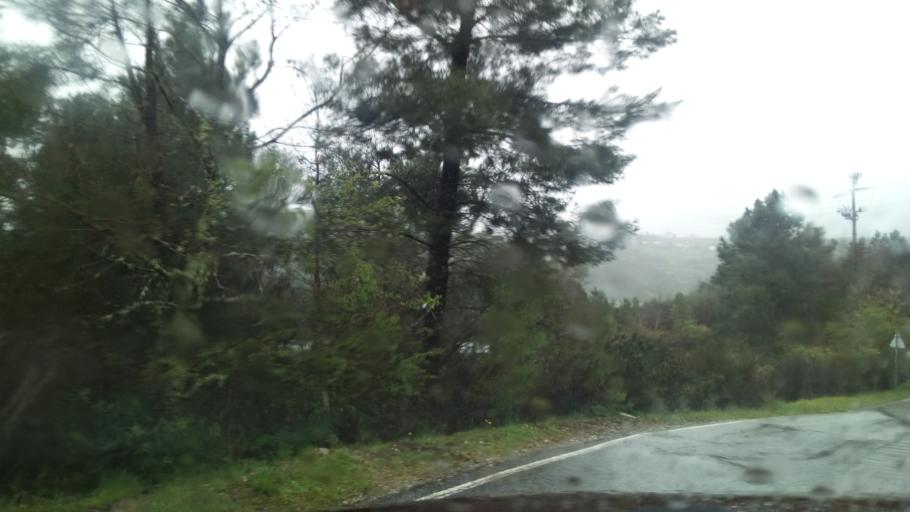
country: PT
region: Guarda
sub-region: Fornos de Algodres
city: Fornos de Algodres
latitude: 40.6198
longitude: -7.5199
